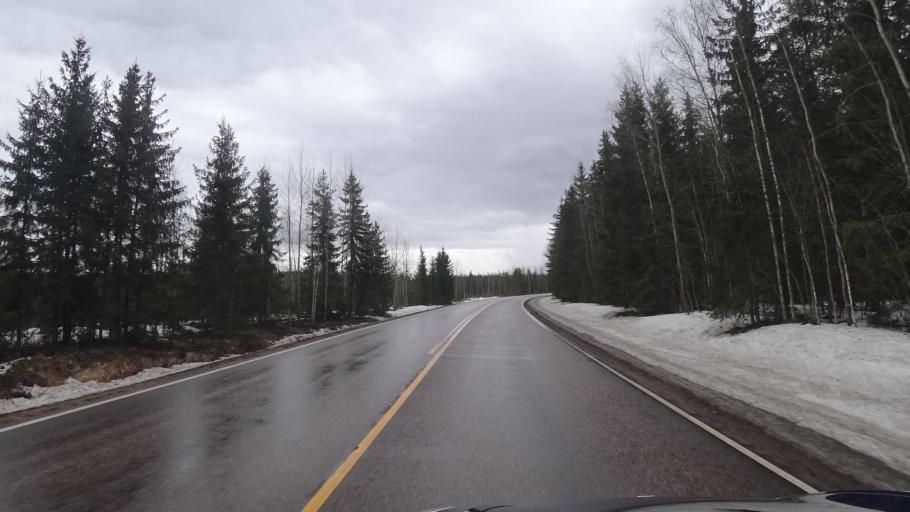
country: FI
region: Uusimaa
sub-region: Loviisa
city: Lapinjaervi
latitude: 60.7322
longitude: 26.2258
